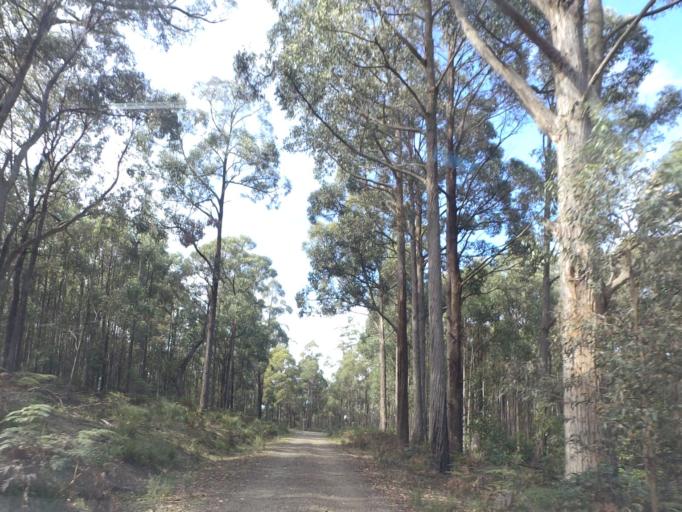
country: AU
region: Victoria
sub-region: Moorabool
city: Bacchus Marsh
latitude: -37.4382
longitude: 144.2716
